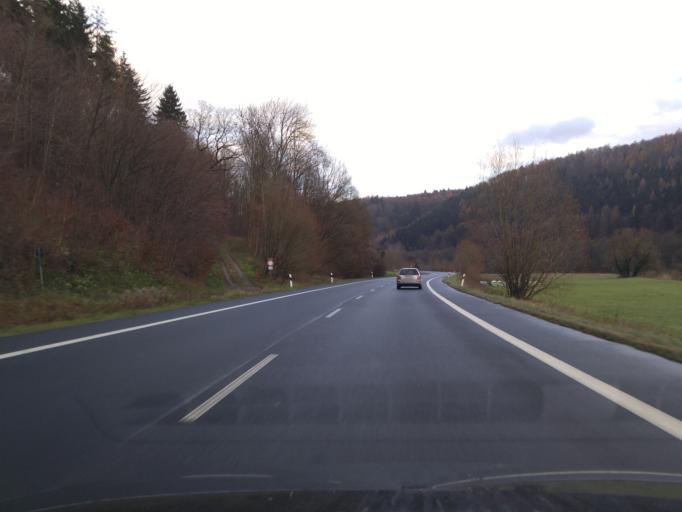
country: DE
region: Lower Saxony
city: Hannoversch Munden
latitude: 51.4134
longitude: 9.6833
